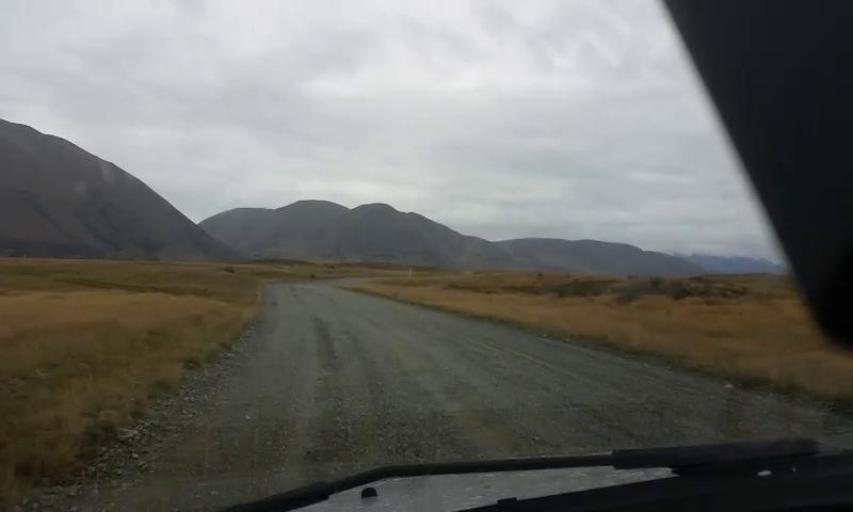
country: NZ
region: Canterbury
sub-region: Ashburton District
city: Methven
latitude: -43.6149
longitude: 171.1079
